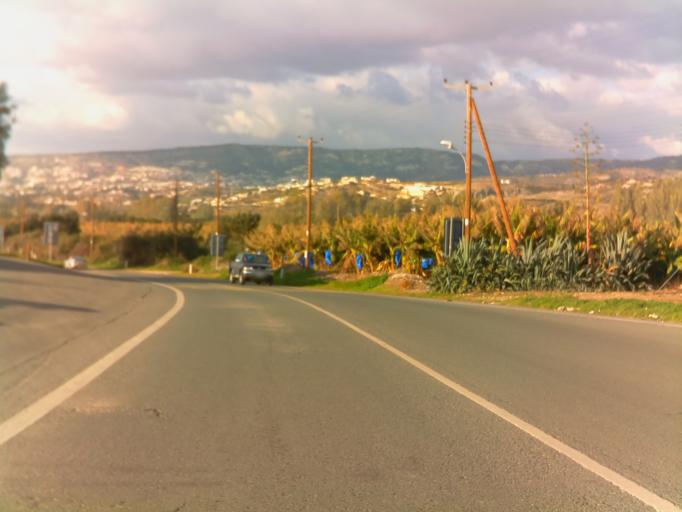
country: CY
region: Pafos
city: Kissonerga
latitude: 34.8321
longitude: 32.3930
